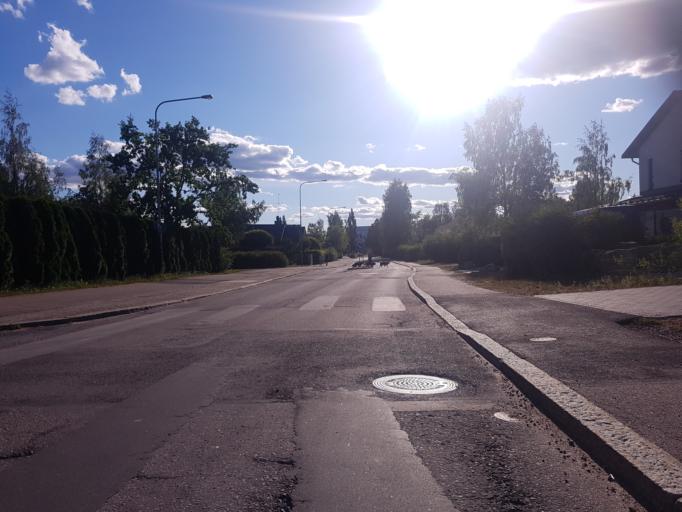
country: FI
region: Uusimaa
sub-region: Helsinki
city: Vantaa
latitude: 60.2678
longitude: 24.9984
